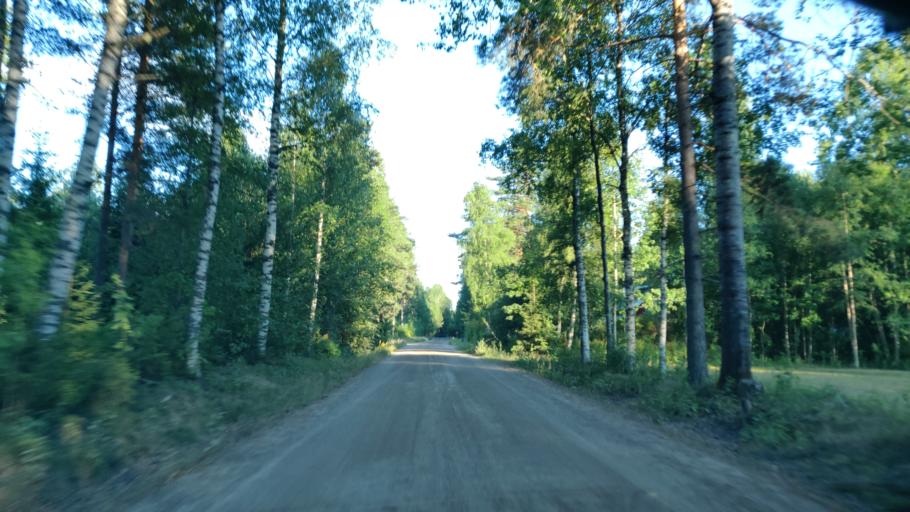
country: SE
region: Vaermland
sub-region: Hagfors Kommun
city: Ekshaerad
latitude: 60.1639
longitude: 13.5065
